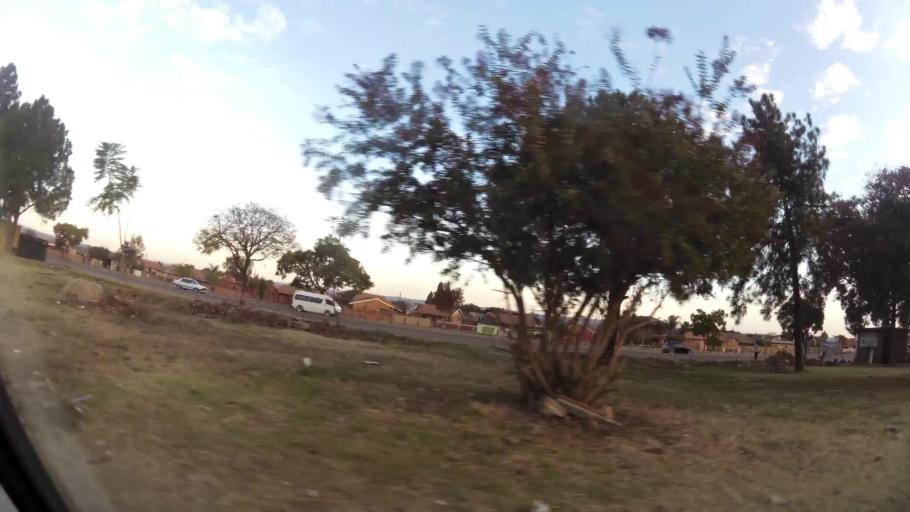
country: ZA
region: Gauteng
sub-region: City of Tshwane Metropolitan Municipality
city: Pretoria
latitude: -25.7180
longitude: 28.3471
